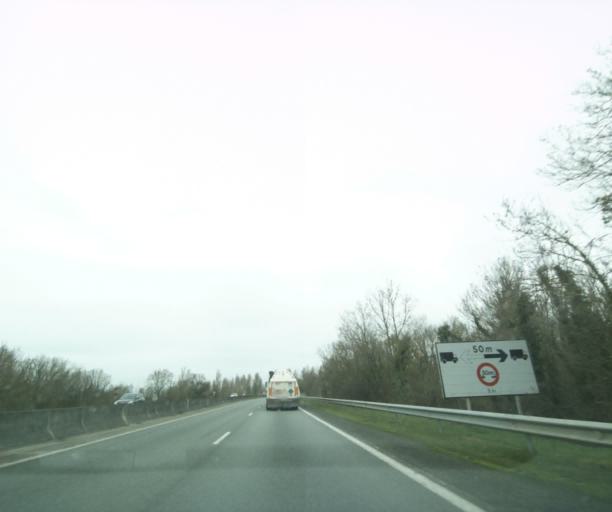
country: FR
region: Poitou-Charentes
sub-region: Departement de la Charente-Maritime
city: Angoulins
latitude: 46.1199
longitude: -1.1086
